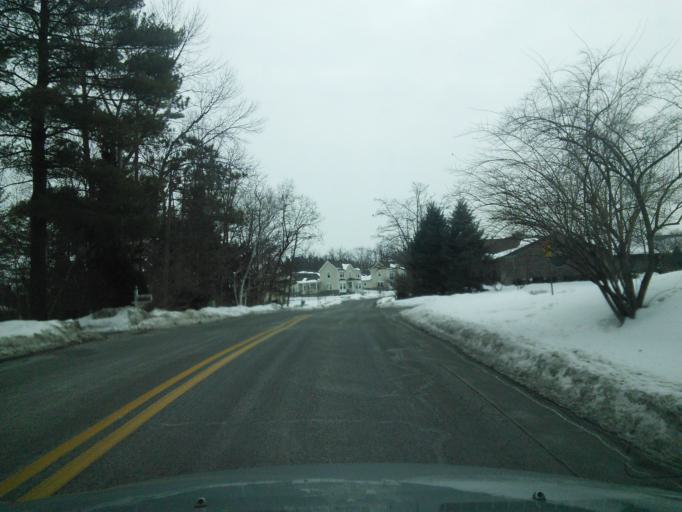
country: US
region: Pennsylvania
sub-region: Centre County
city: State College
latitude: 40.8287
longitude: -77.8807
